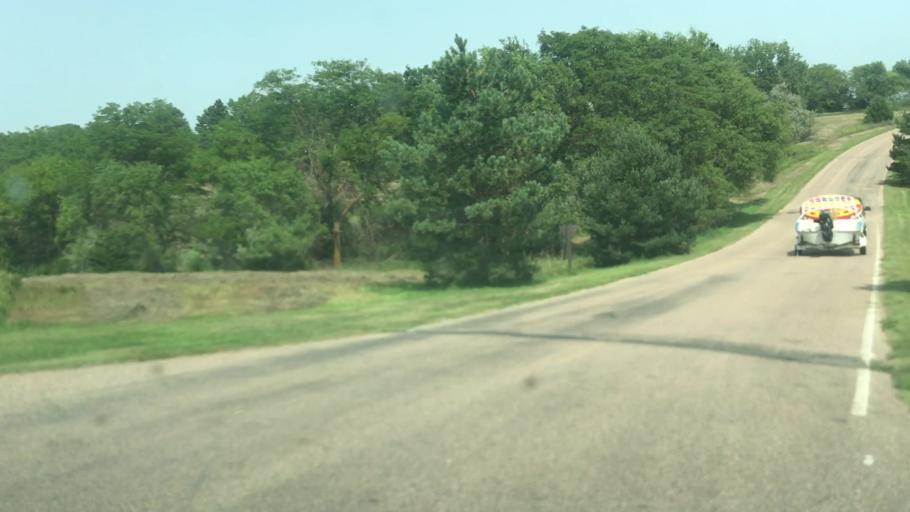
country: US
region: Nebraska
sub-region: Sherman County
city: Loup City
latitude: 41.2876
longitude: -98.8997
